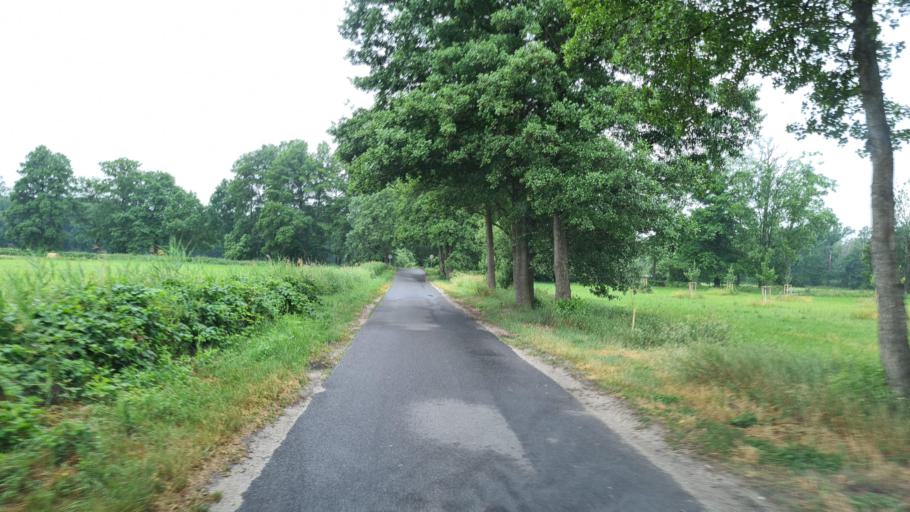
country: DE
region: Brandenburg
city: Lindenau
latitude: 51.3945
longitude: 13.7268
